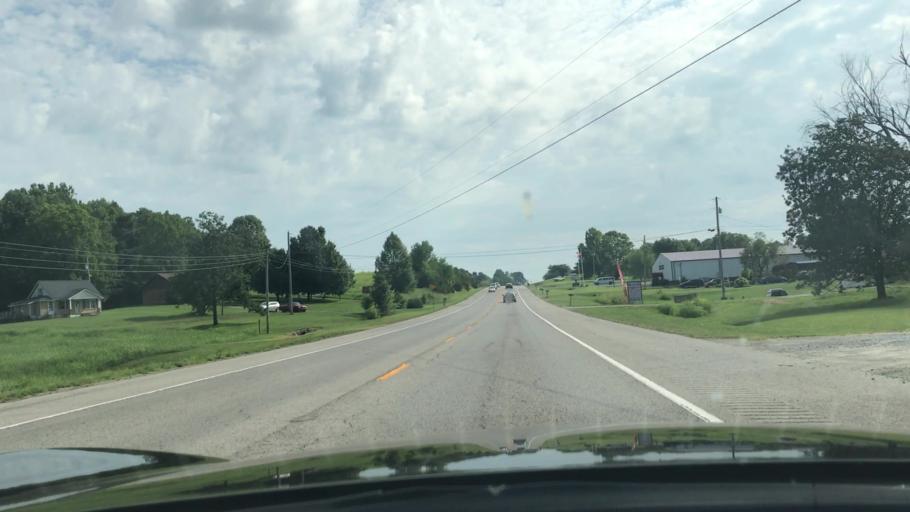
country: US
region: Kentucky
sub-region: Green County
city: Greensburg
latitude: 37.2853
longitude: -85.4837
